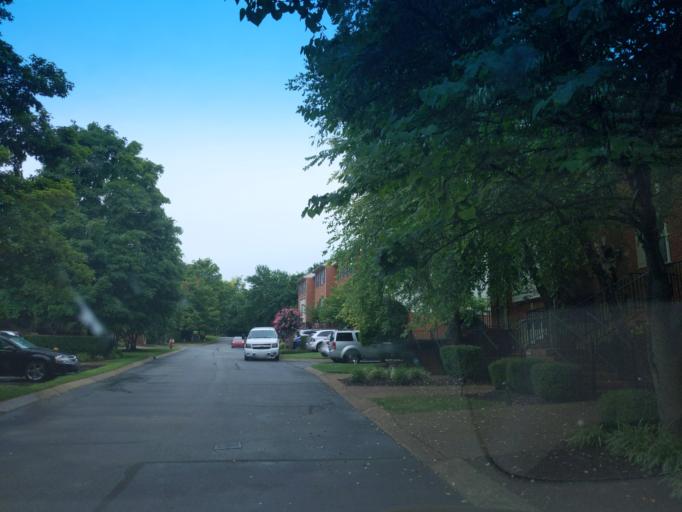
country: US
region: Tennessee
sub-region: Williamson County
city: Brentwood
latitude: 36.0372
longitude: -86.7638
